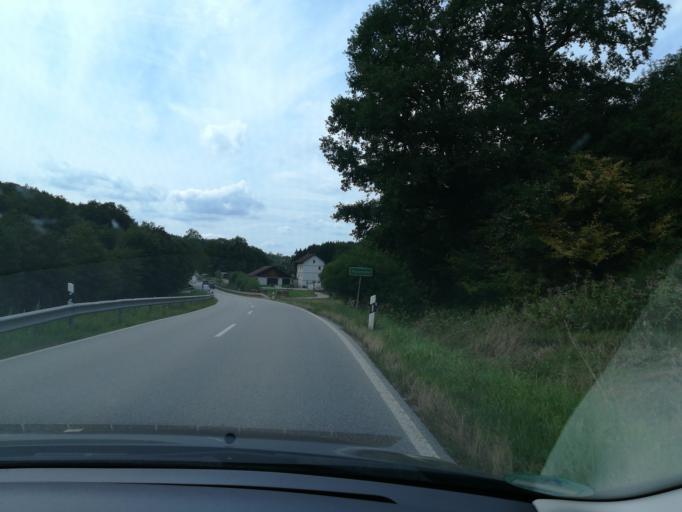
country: DE
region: Bavaria
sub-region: Upper Bavaria
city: Assling
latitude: 47.9861
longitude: 11.9635
